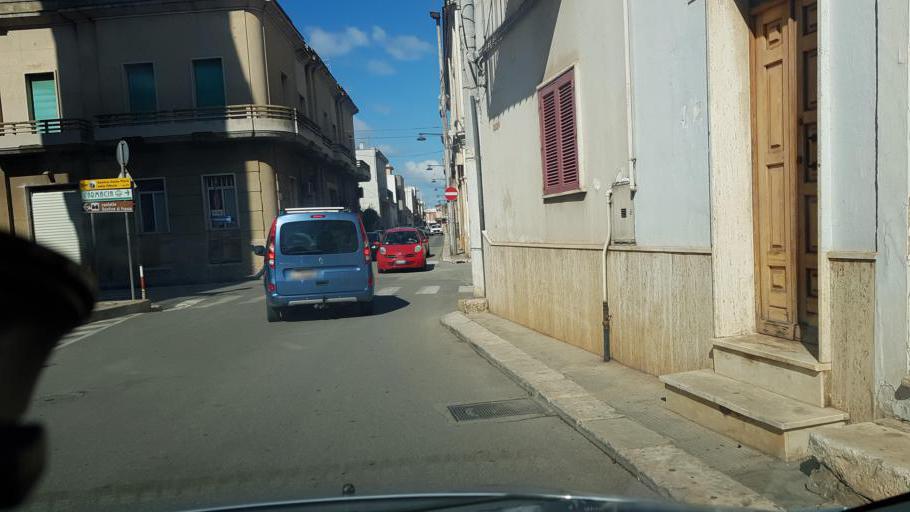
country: IT
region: Apulia
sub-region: Provincia di Brindisi
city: San Vito dei Normanni
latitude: 40.6565
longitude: 17.7076
